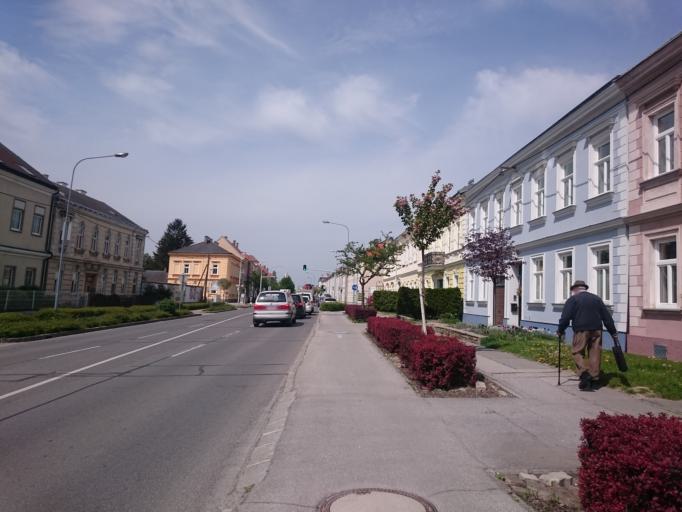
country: AT
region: Lower Austria
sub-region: Politischer Bezirk Korneuburg
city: Korneuburg
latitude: 48.3476
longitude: 16.3288
